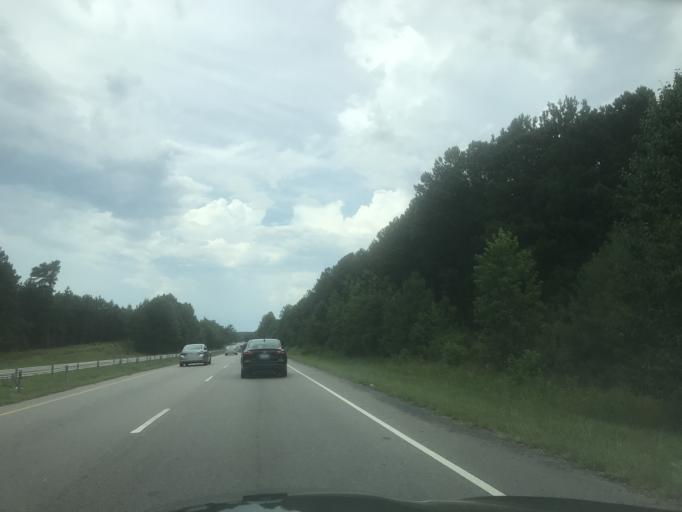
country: US
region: North Carolina
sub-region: Johnston County
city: Clayton
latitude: 35.6778
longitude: -78.5242
